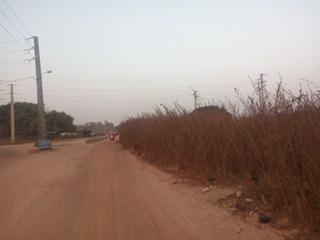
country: BJ
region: Borgou
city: Parakou
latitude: 9.3264
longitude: 2.5954
